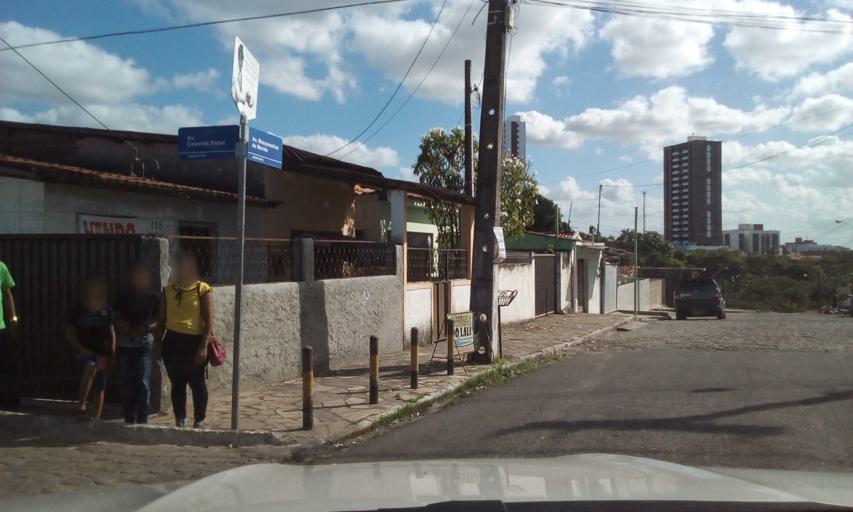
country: BR
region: Paraiba
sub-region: Joao Pessoa
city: Joao Pessoa
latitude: -7.1074
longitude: -34.8625
